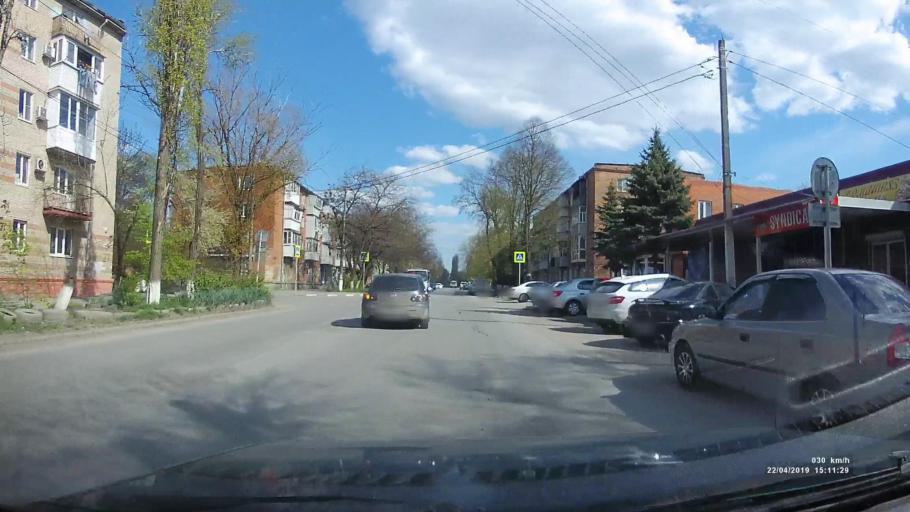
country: RU
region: Rostov
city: Azov
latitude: 47.1002
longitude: 39.4157
